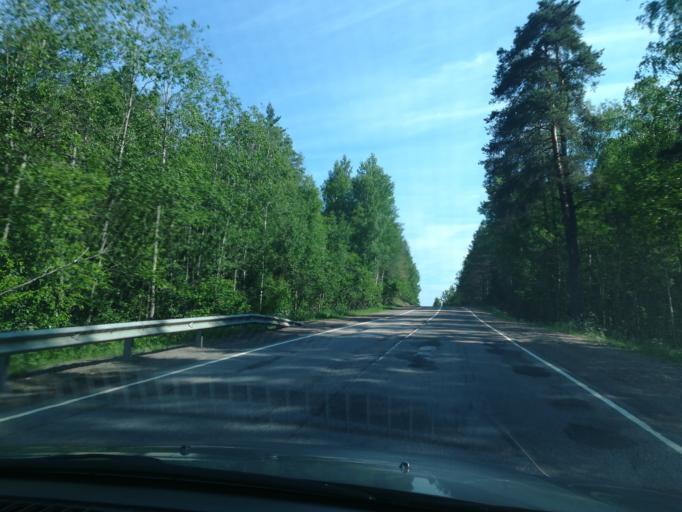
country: RU
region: Leningrad
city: Lesogorskiy
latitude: 60.9123
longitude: 28.8855
